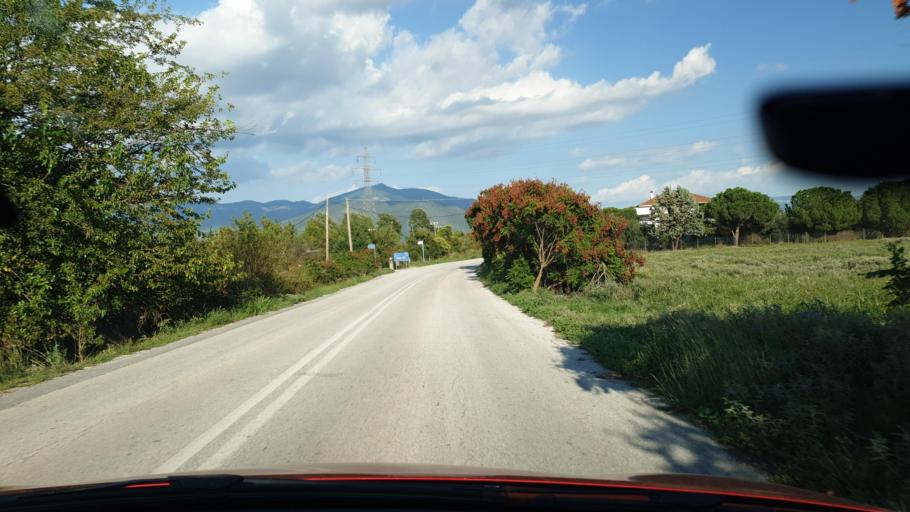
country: GR
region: Central Macedonia
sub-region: Nomos Thessalonikis
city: Souroti
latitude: 40.4757
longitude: 23.0994
